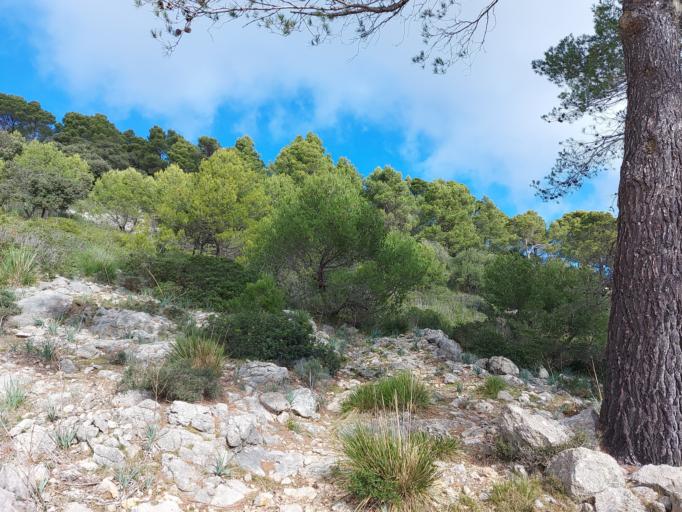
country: ES
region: Balearic Islands
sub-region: Illes Balears
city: Fornalutx
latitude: 39.7956
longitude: 2.7392
